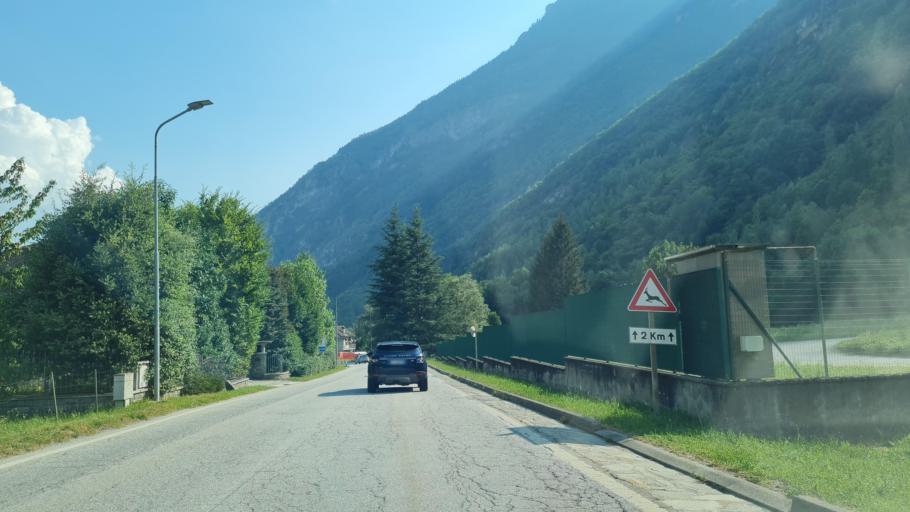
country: IT
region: Piedmont
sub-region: Provincia Verbano-Cusio-Ossola
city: Crodo
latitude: 46.2075
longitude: 8.3193
